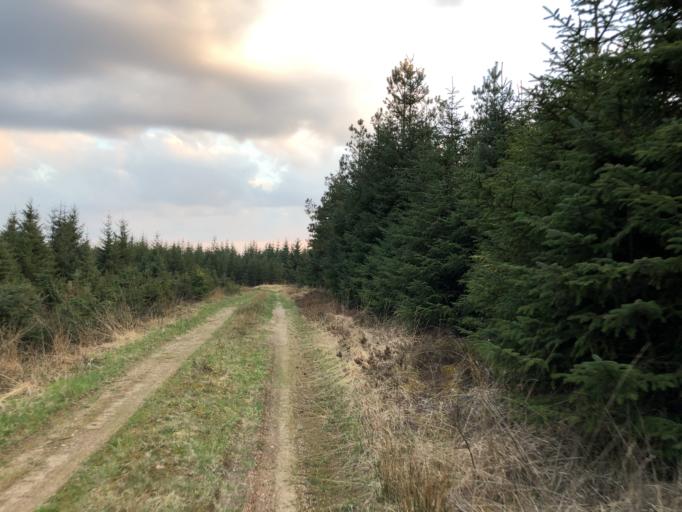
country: DK
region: Central Jutland
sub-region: Holstebro Kommune
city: Ulfborg
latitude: 56.2266
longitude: 8.4279
